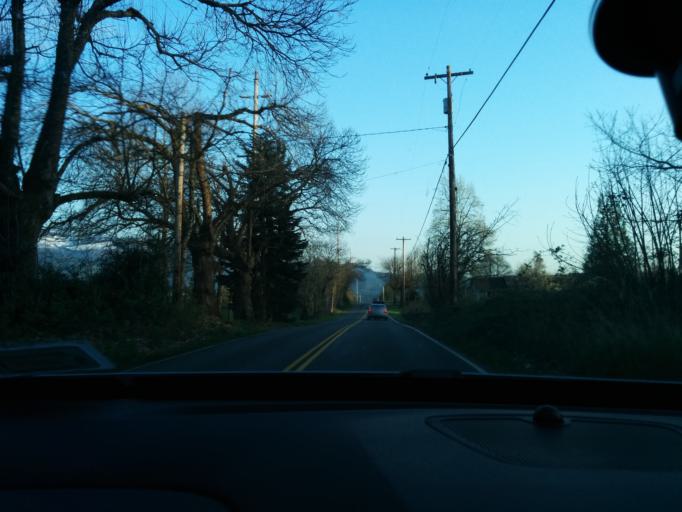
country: US
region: Washington
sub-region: Snohomish County
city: Sultan
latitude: 47.8941
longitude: -121.7991
